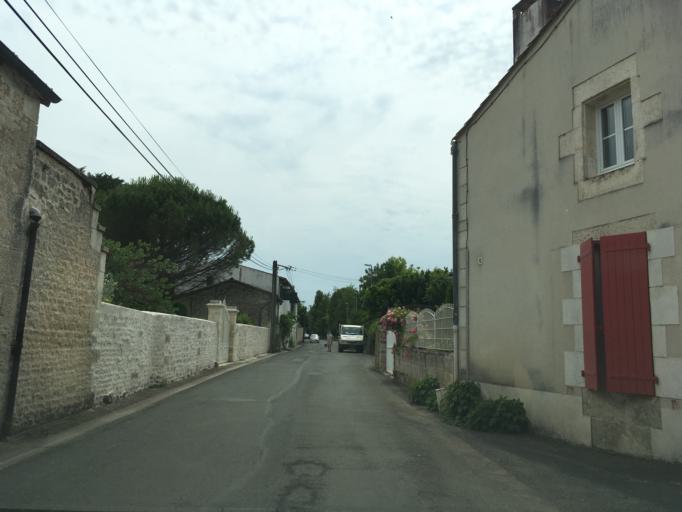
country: FR
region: Poitou-Charentes
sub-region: Departement des Deux-Sevres
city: Bessines
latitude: 46.3277
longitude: -0.5101
